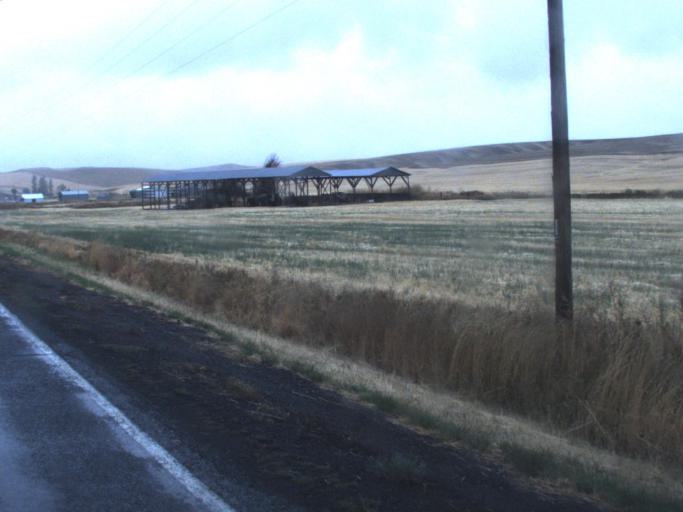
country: US
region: Washington
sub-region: Whitman County
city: Colfax
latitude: 47.0110
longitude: -117.4747
